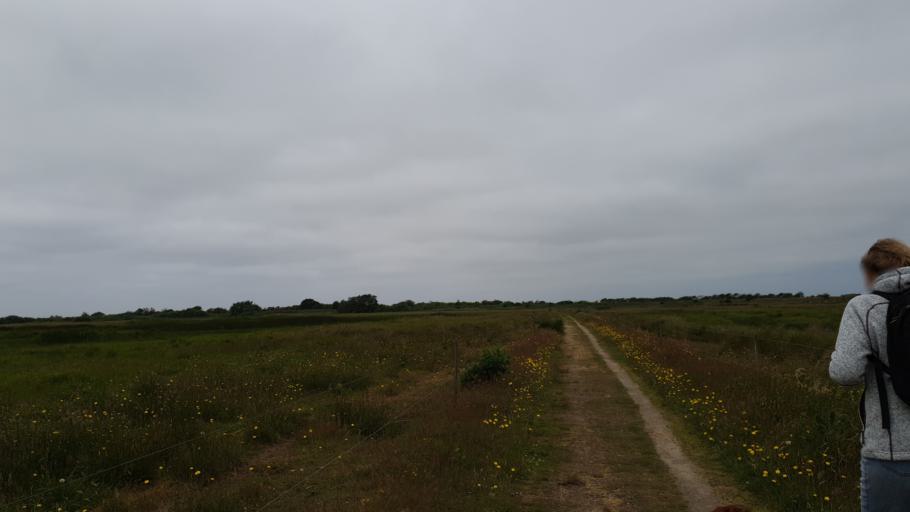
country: DK
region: Central Jutland
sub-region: Ringkobing-Skjern Kommune
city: Skjern
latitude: 55.9150
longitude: 8.4068
